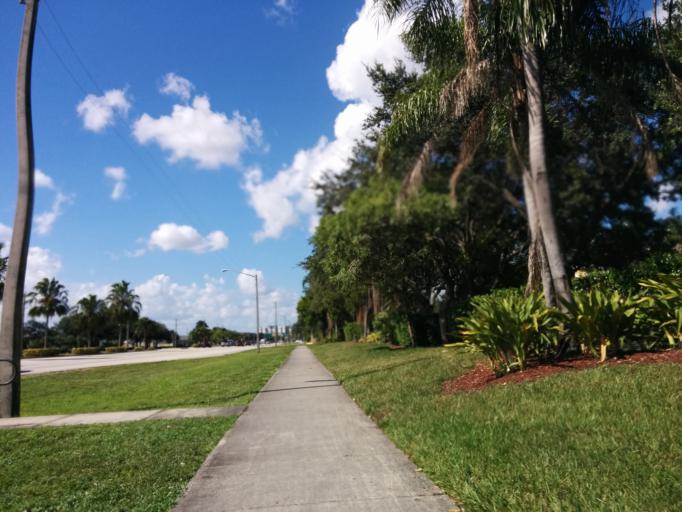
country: US
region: Florida
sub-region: Broward County
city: Pine Island Ridge
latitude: 26.0873
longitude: -80.2507
